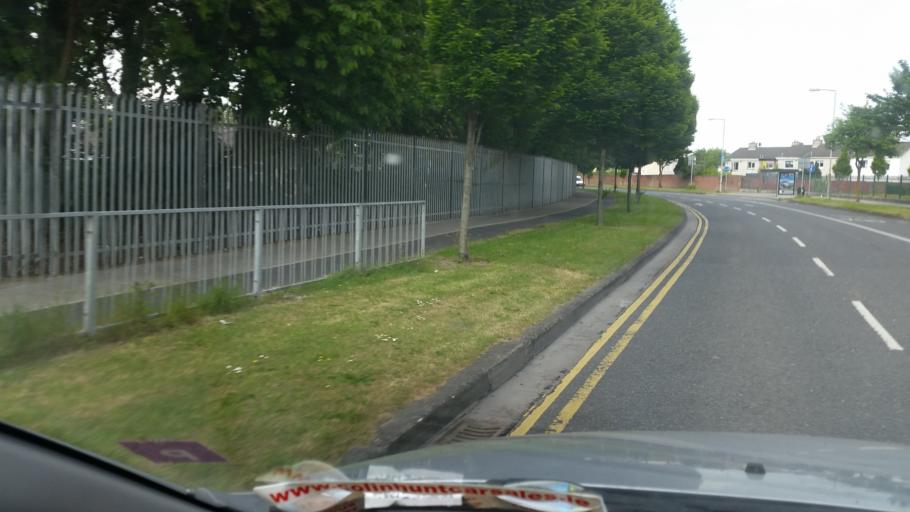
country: IE
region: Leinster
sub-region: Fingal County
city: Blanchardstown
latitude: 53.3971
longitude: -6.3995
